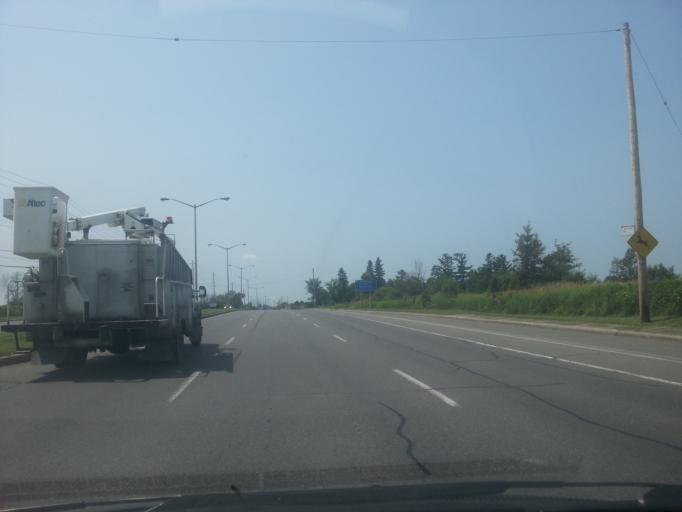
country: CA
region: Ontario
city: Ottawa
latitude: 45.4230
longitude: -75.5866
